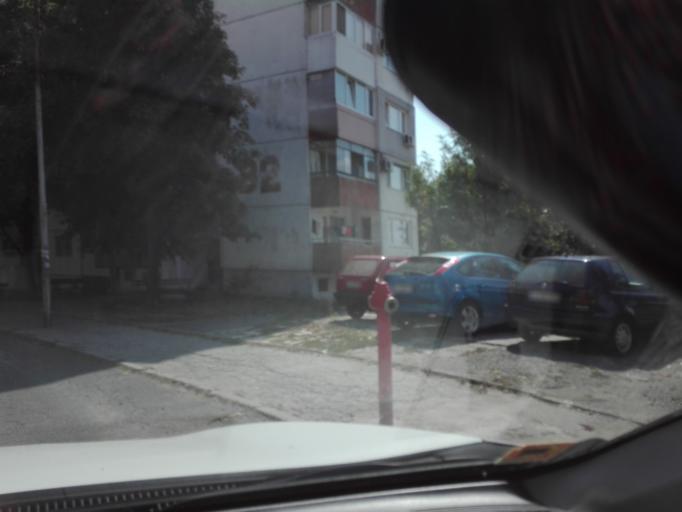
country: BG
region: Burgas
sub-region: Obshtina Burgas
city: Burgas
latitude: 42.4584
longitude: 27.4175
